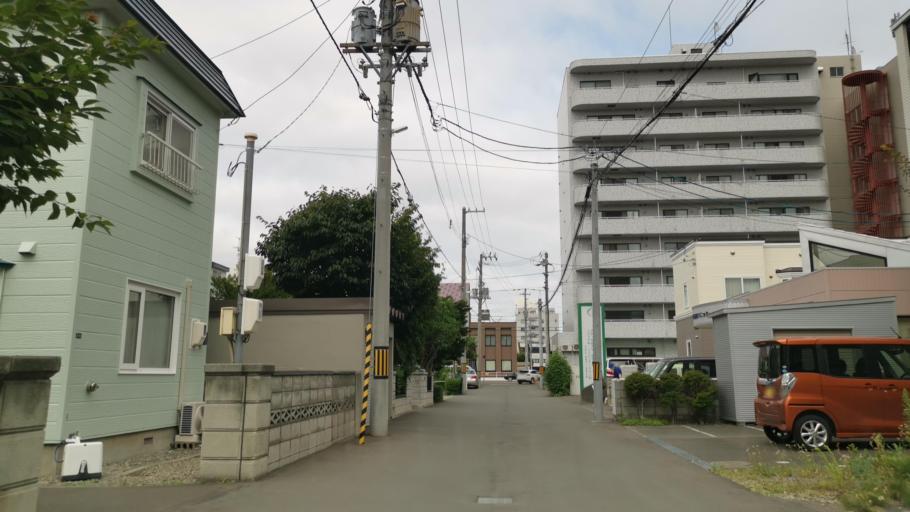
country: JP
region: Hokkaido
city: Sapporo
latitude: 43.0468
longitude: 141.3346
